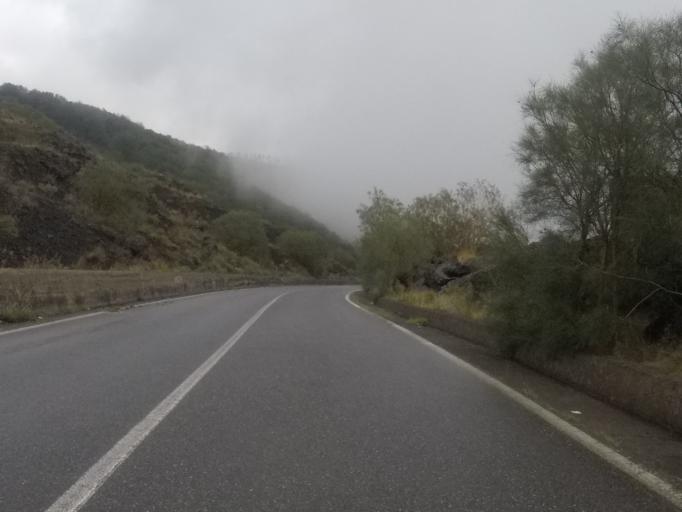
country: IT
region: Sicily
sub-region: Catania
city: Nicolosi
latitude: 37.6661
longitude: 15.0299
